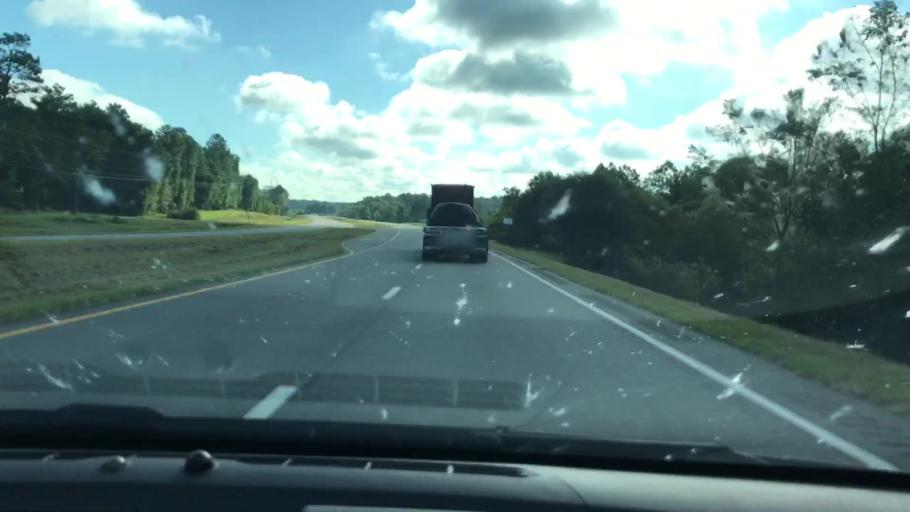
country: US
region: Georgia
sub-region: Worth County
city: Sylvester
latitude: 31.5501
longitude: -83.9640
